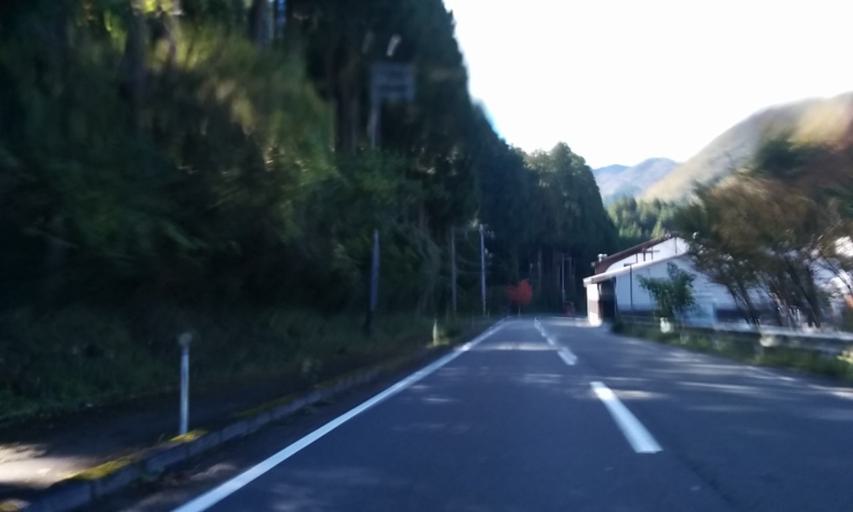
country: JP
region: Kyoto
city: Kameoka
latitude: 35.2597
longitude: 135.5550
